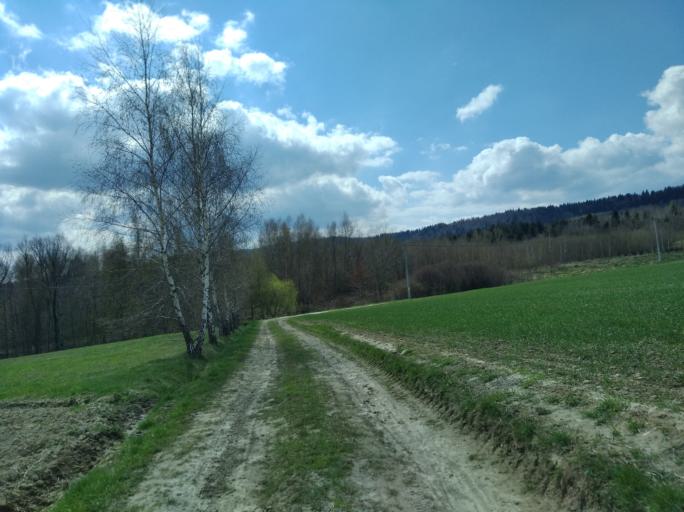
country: PL
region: Subcarpathian Voivodeship
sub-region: Powiat strzyzowski
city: Strzyzow
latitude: 49.8396
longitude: 21.7808
